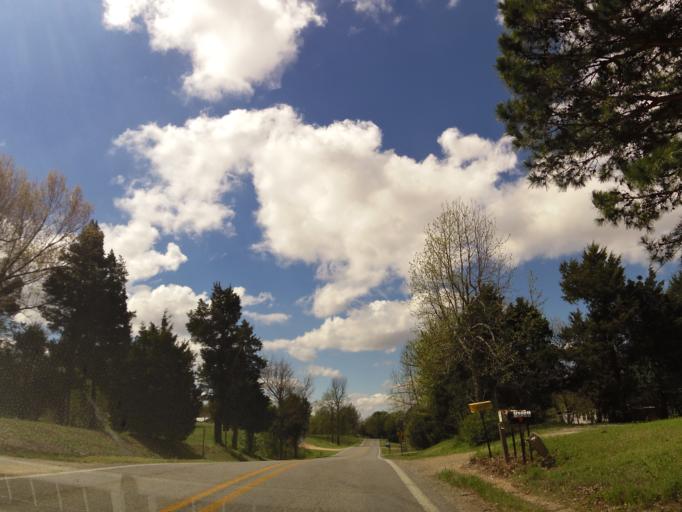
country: US
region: Arkansas
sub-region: Craighead County
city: Brookland
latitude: 36.0362
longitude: -90.6733
